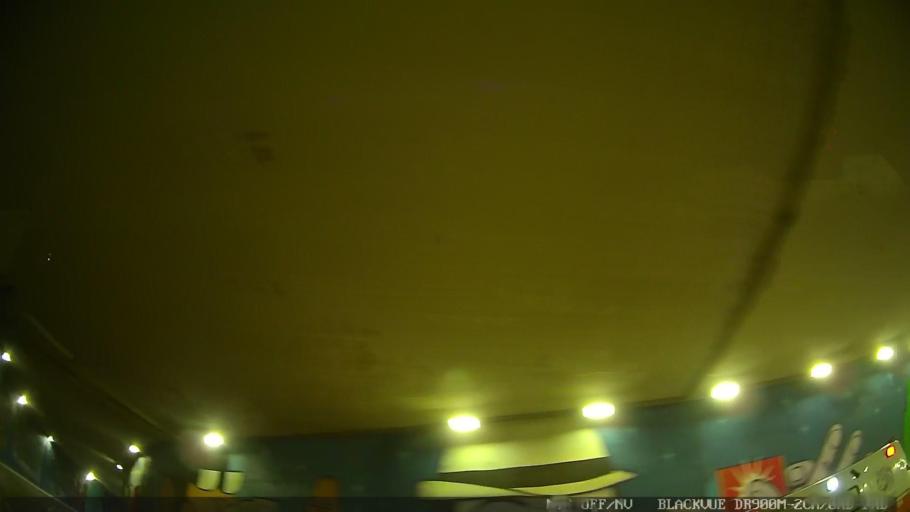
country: BR
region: Sao Paulo
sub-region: Sao Paulo
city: Sao Paulo
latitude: -23.5585
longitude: -46.6728
